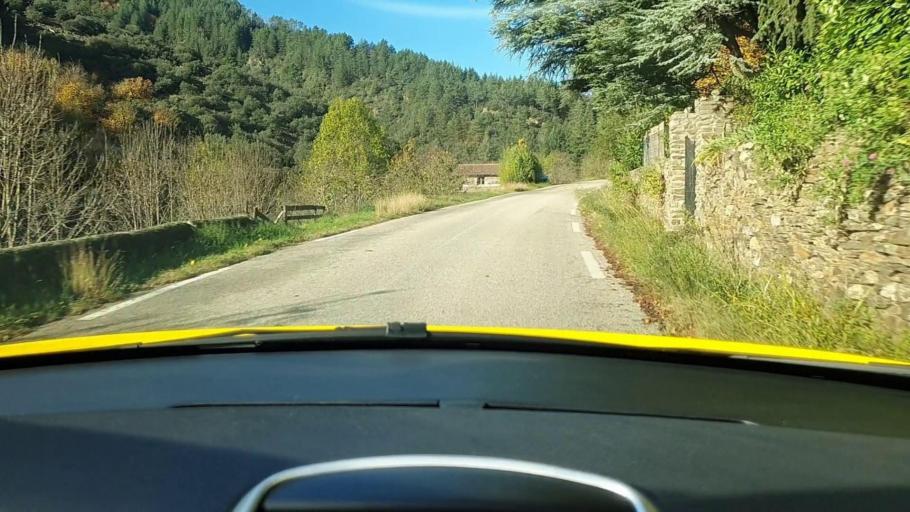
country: FR
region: Languedoc-Roussillon
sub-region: Departement du Gard
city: Valleraugue
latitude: 44.1394
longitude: 3.7059
